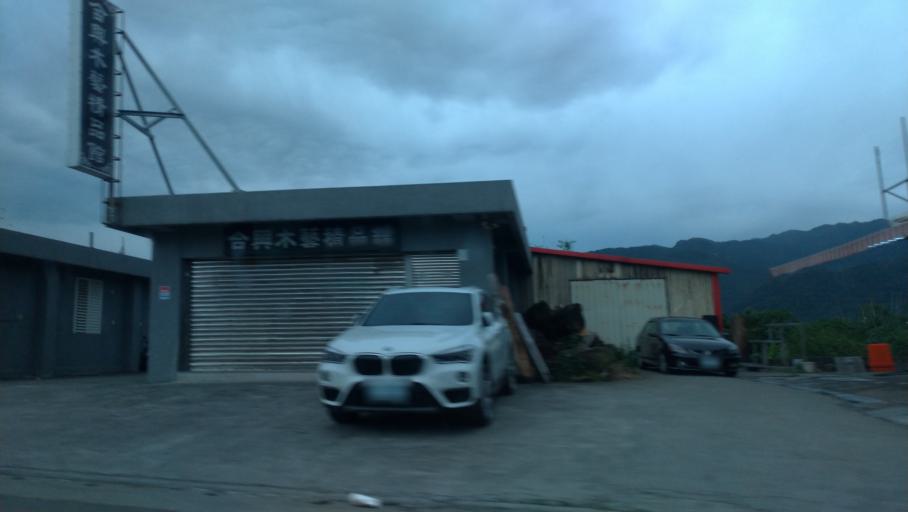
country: TW
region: Taiwan
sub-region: Yilan
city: Yilan
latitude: 24.8491
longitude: 121.8147
